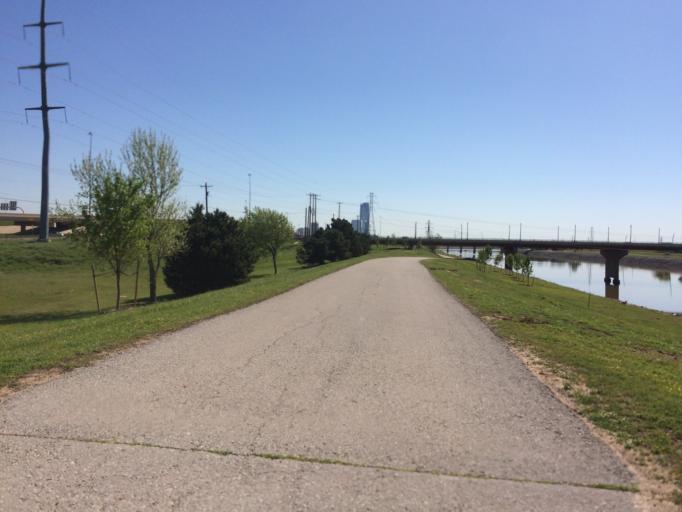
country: US
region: Oklahoma
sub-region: Oklahoma County
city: Oklahoma City
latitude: 35.4599
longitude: -97.5572
